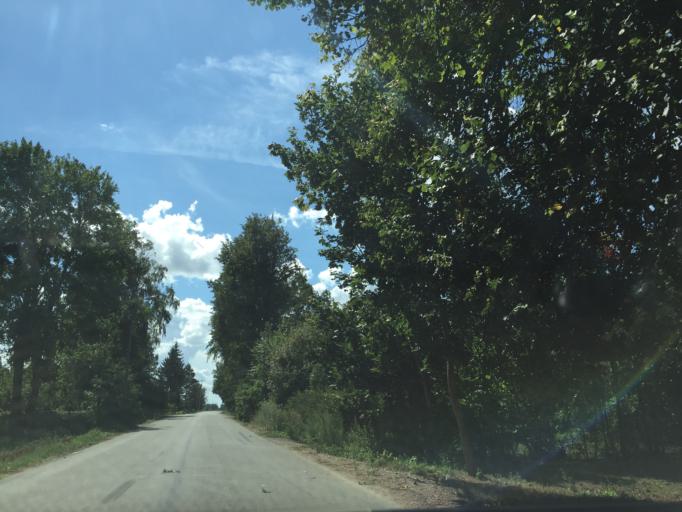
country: LV
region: Rundales
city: Pilsrundale
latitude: 56.3141
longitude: 23.9109
